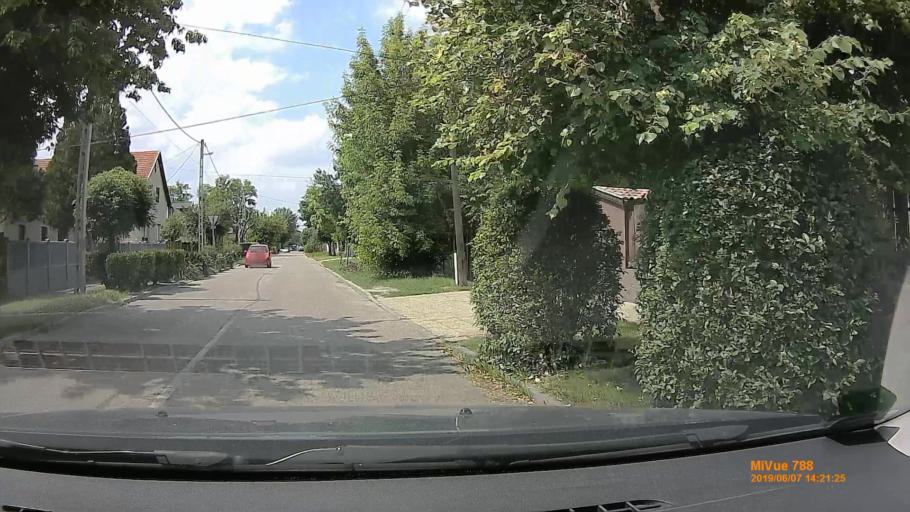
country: HU
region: Budapest
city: Budapest XIX. keruelet
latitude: 47.4328
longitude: 19.1364
